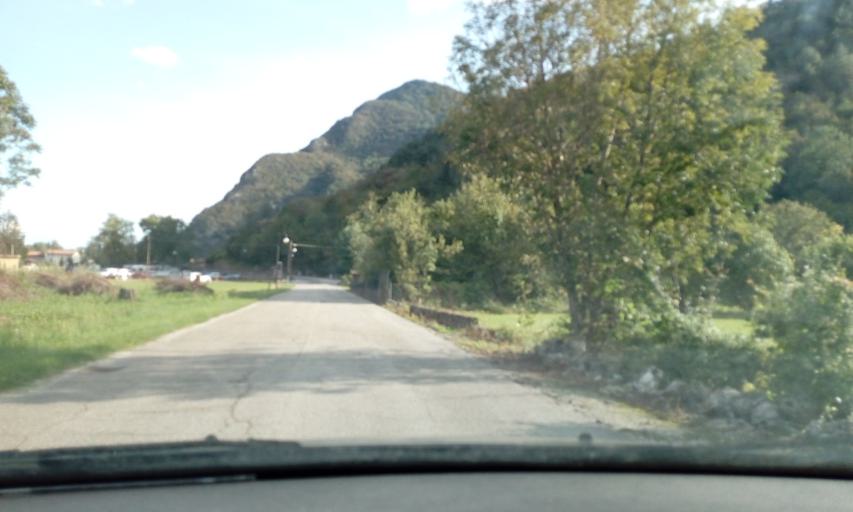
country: IT
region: Friuli Venezia Giulia
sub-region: Provincia di Udine
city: Trasaghis
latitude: 46.2988
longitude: 13.0506
